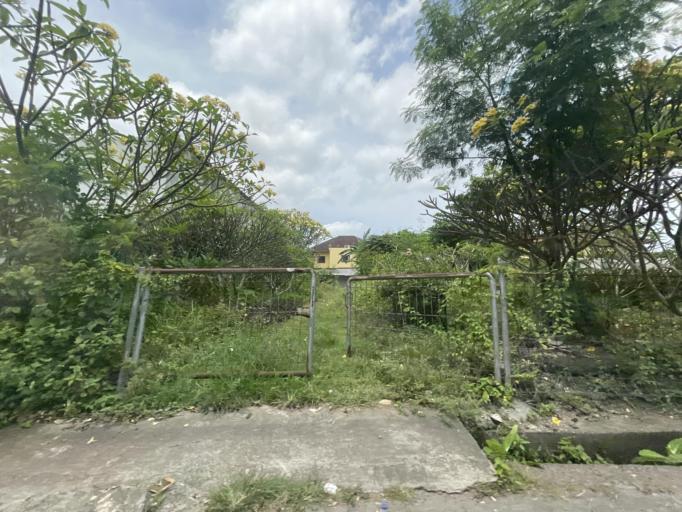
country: ID
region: Bali
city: Banjar Kerobokan
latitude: -8.6648
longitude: 115.1413
